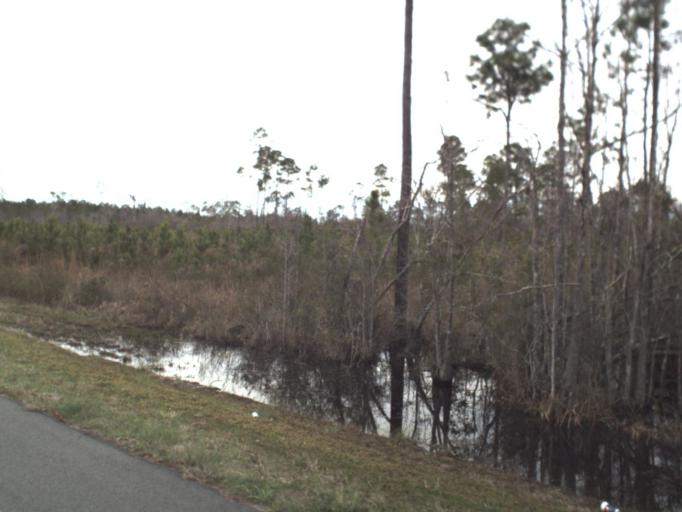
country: US
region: Florida
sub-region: Gulf County
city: Wewahitchka
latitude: 30.1388
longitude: -85.2502
